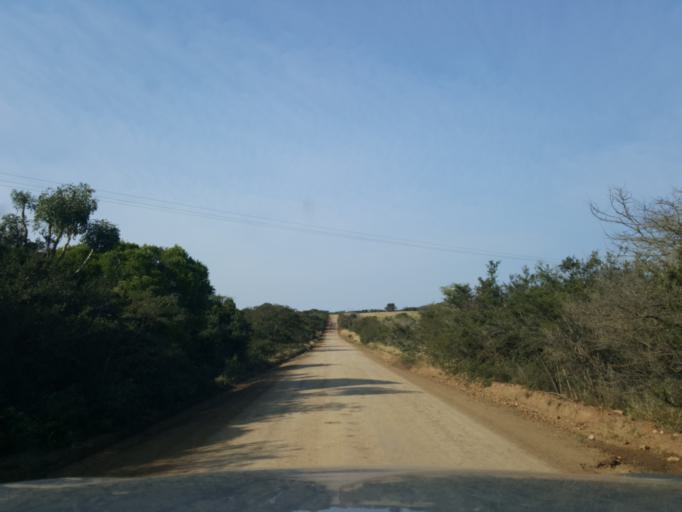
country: ZA
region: Eastern Cape
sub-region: Cacadu District Municipality
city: Grahamstown
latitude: -33.4055
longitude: 26.2964
